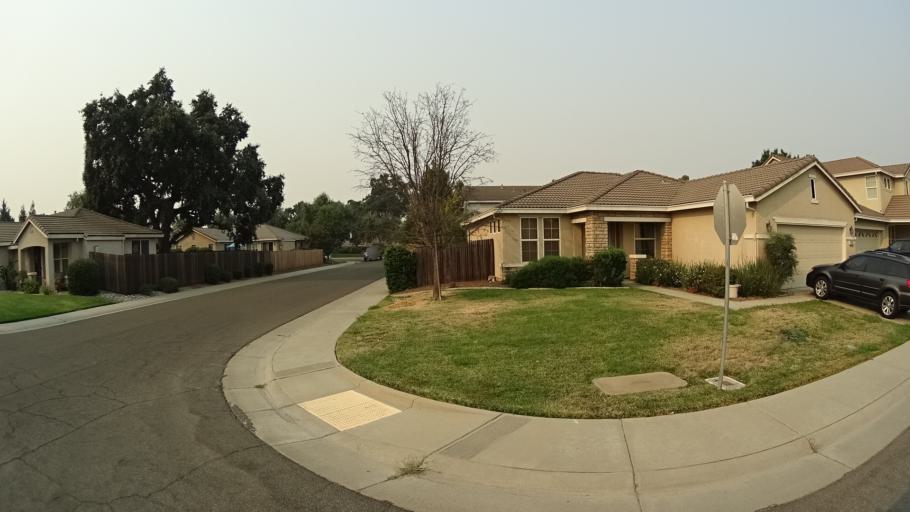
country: US
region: California
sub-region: Sacramento County
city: Laguna
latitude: 38.4038
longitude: -121.4483
